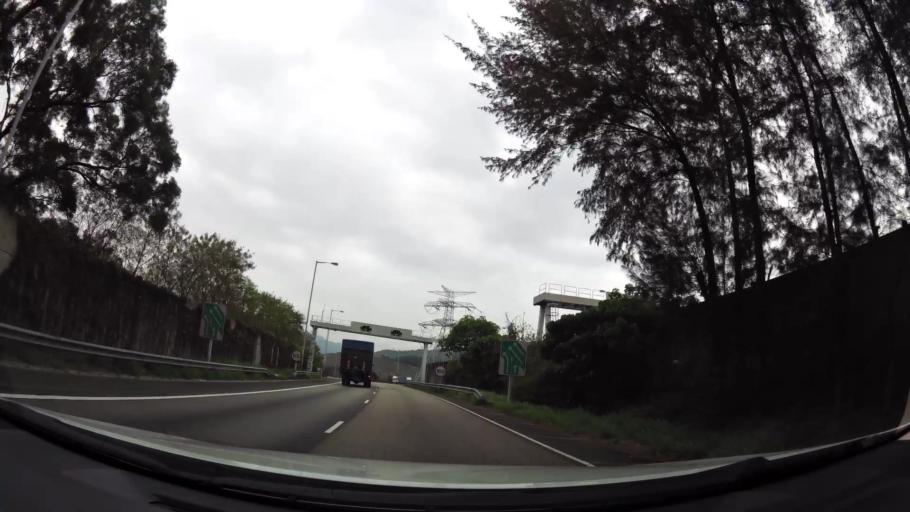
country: HK
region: Yuen Long
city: Yuen Long Kau Hui
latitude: 22.4435
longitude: 114.0511
